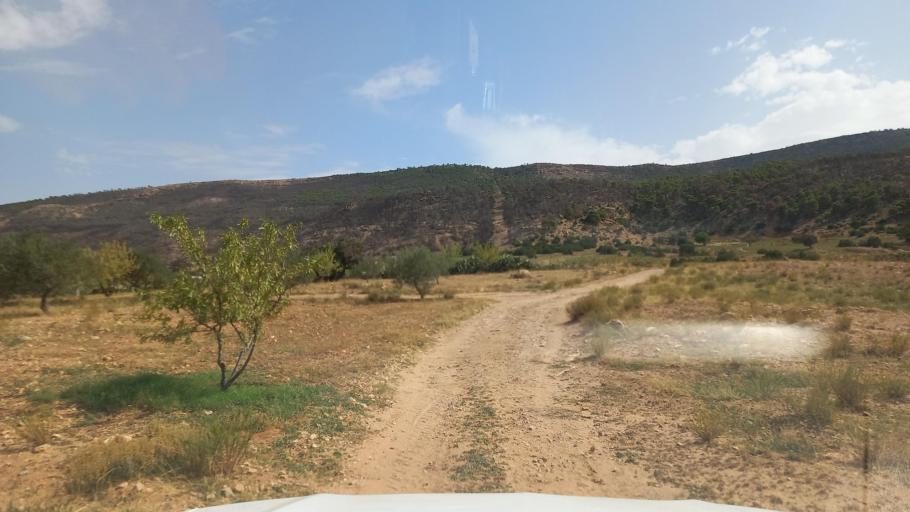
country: TN
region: Al Qasrayn
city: Kasserine
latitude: 35.3557
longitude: 8.8894
